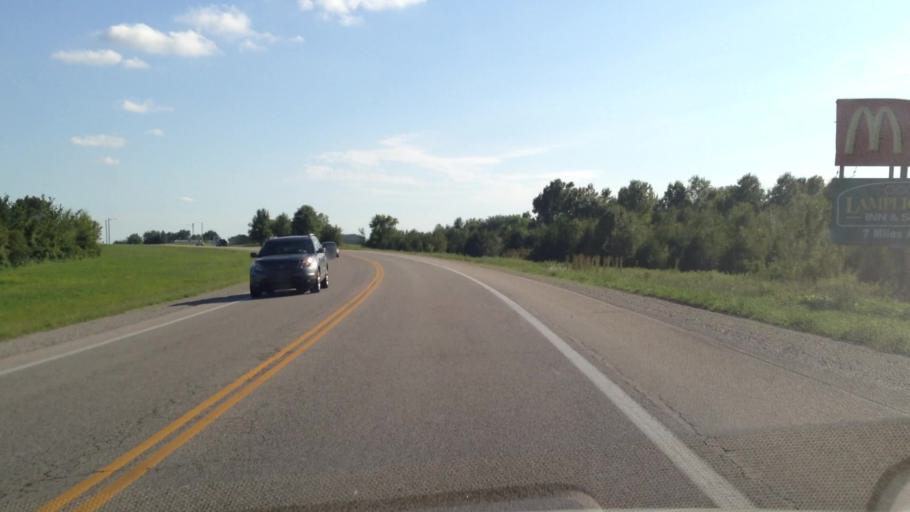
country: US
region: Kansas
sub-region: Crawford County
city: Arma
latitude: 37.5503
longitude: -94.7098
